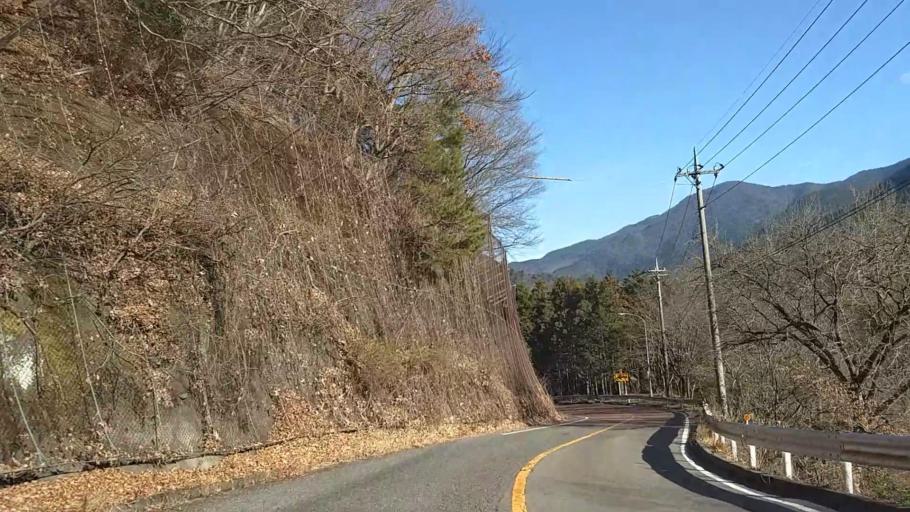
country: JP
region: Yamanashi
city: Uenohara
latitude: 35.5317
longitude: 139.1040
